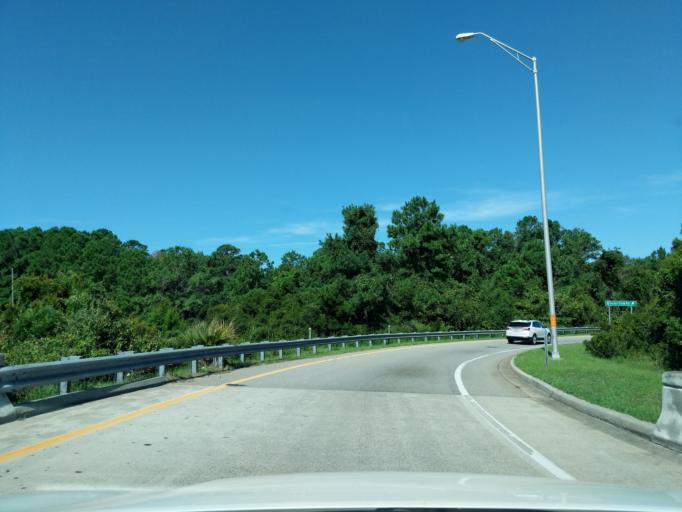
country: US
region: South Carolina
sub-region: Charleston County
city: Charleston
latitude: 32.7557
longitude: -79.9613
